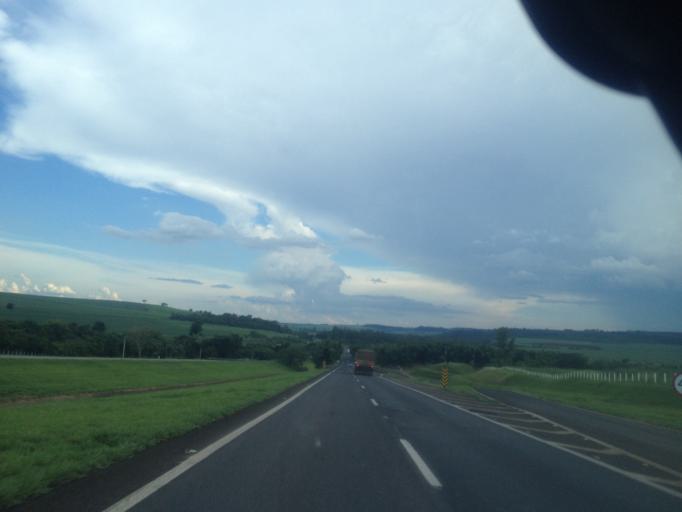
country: BR
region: Sao Paulo
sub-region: Santa Rita Do Passa Quatro
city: Santa Rita do Passa Quatro
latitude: -21.7264
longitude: -47.5868
